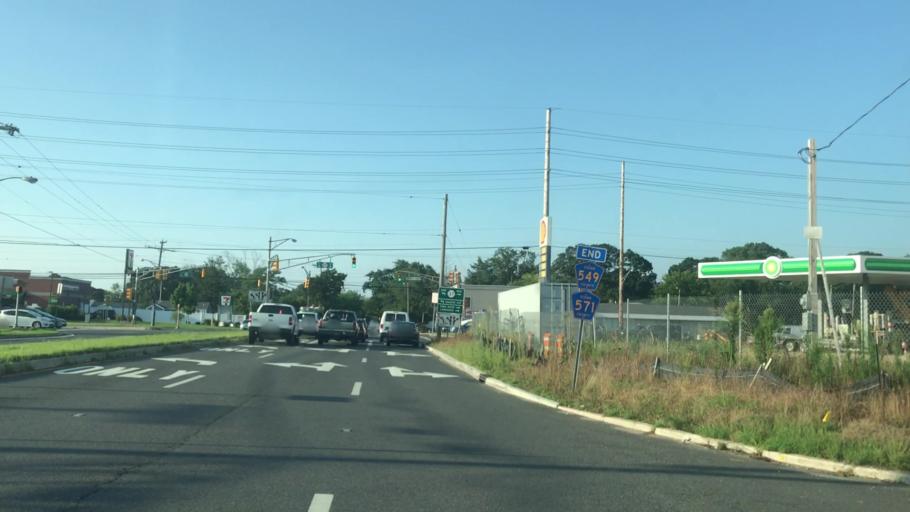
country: US
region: New Jersey
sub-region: Ocean County
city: Ocean Gate
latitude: 39.9507
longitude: -74.1243
